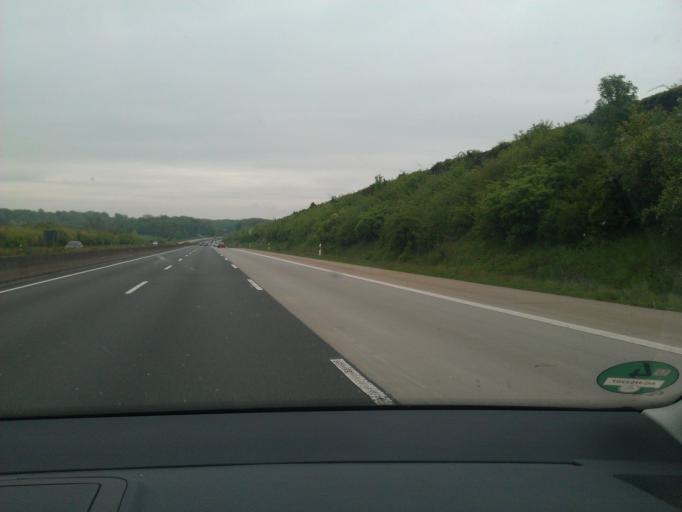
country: DE
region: North Rhine-Westphalia
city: Tuernich
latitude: 50.9138
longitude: 6.7415
